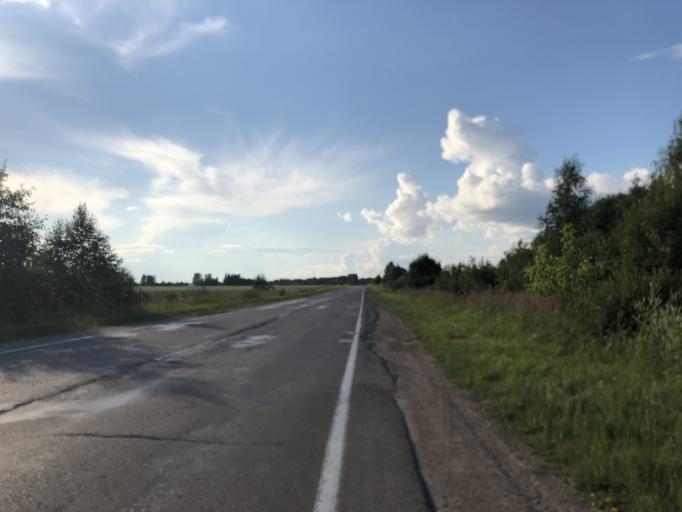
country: RU
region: Tverskaya
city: Rzhev
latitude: 56.2780
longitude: 34.2364
